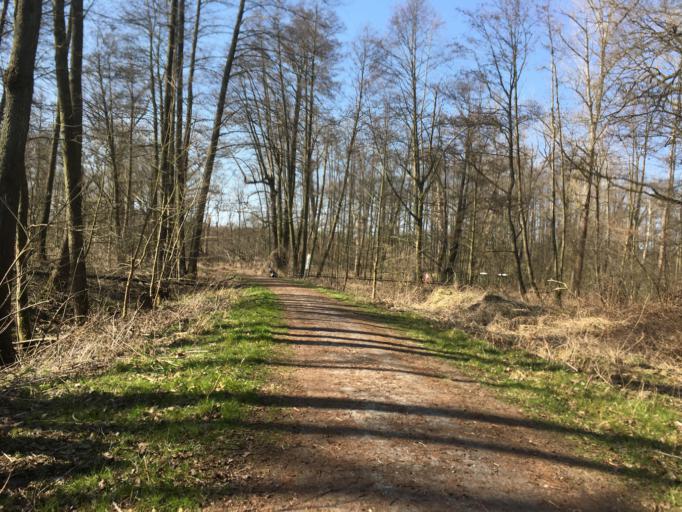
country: DE
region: Berlin
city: Buch
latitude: 52.6393
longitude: 13.4690
